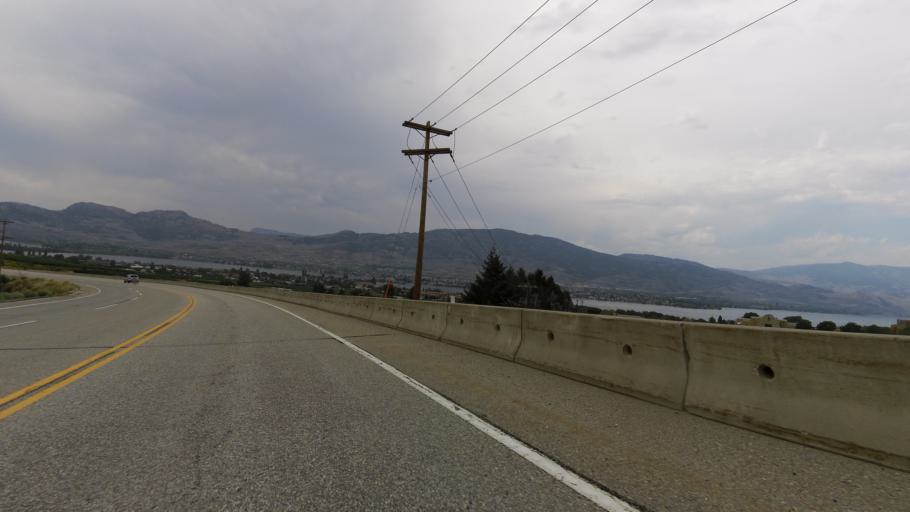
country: CA
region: British Columbia
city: Osoyoos
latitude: 49.0374
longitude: -119.4289
